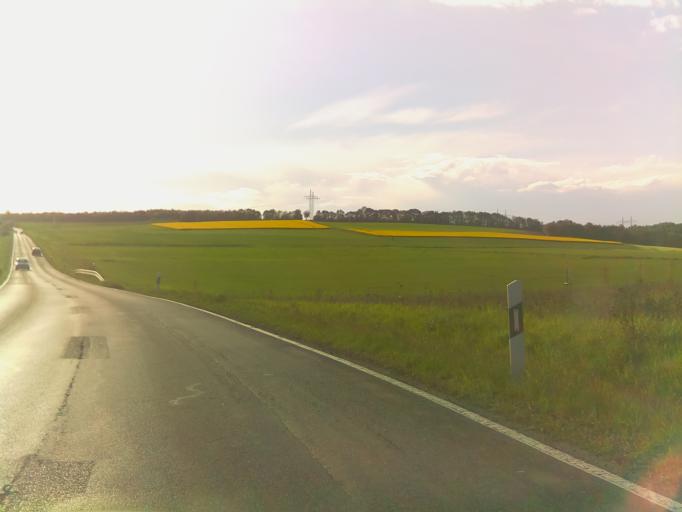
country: DE
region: Bavaria
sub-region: Regierungsbezirk Unterfranken
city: Oerlenbach
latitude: 50.1473
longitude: 10.1277
